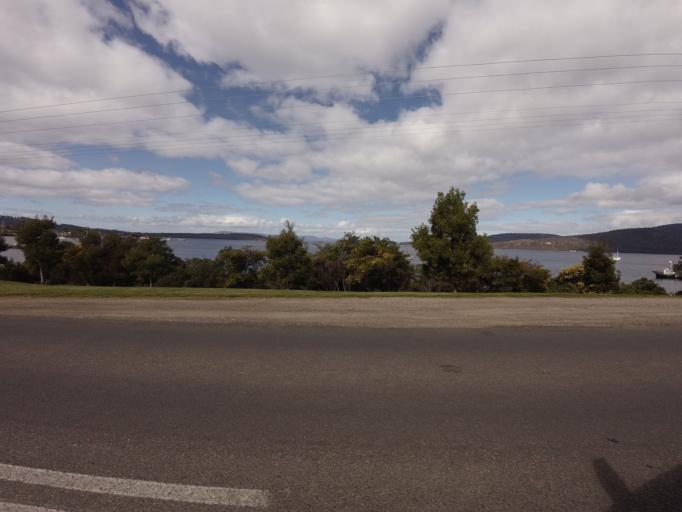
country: AU
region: Tasmania
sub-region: Huon Valley
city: Geeveston
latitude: -43.3189
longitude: 147.0089
